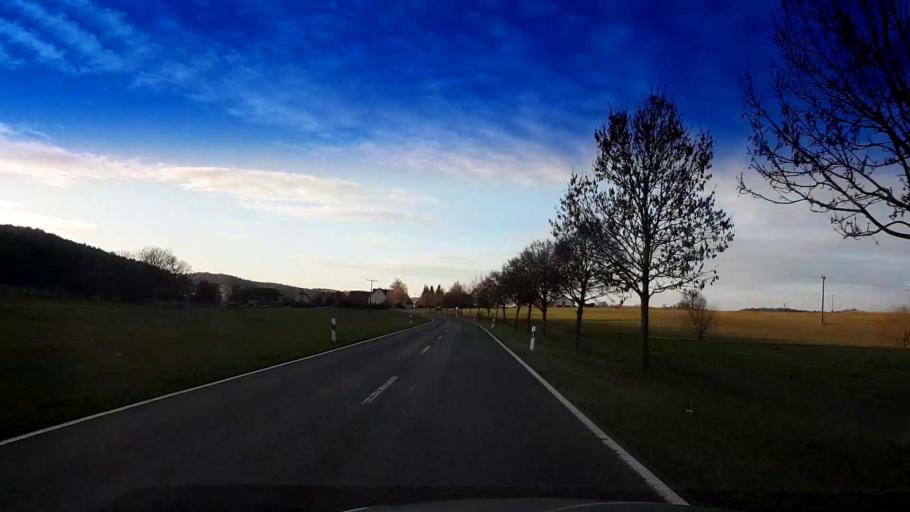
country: DE
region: Bavaria
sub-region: Upper Franconia
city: Walsdorf
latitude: 49.8862
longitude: 10.7541
